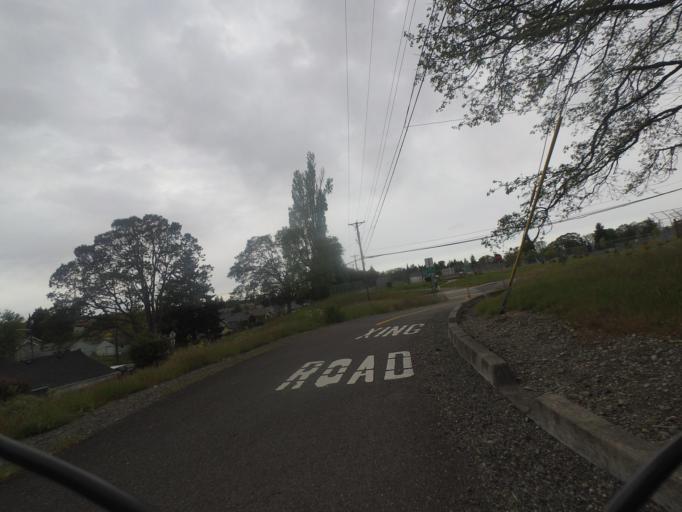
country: US
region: Washington
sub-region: Pierce County
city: Lakewood
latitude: 47.2025
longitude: -122.4765
